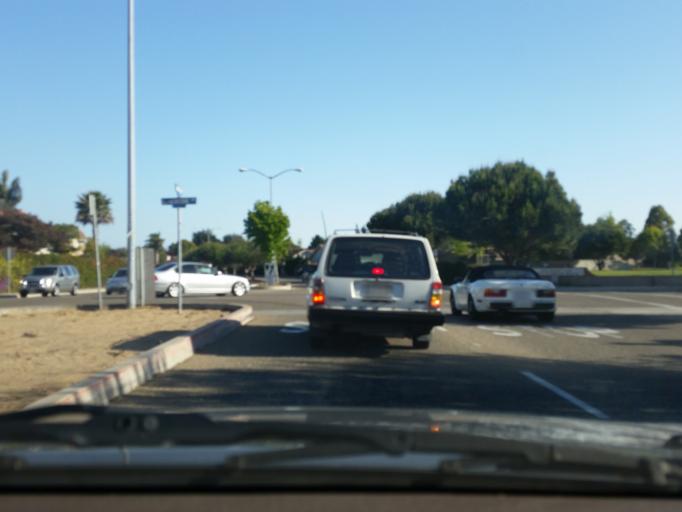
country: US
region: California
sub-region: San Luis Obispo County
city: Grover Beach
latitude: 35.1152
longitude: -120.6096
